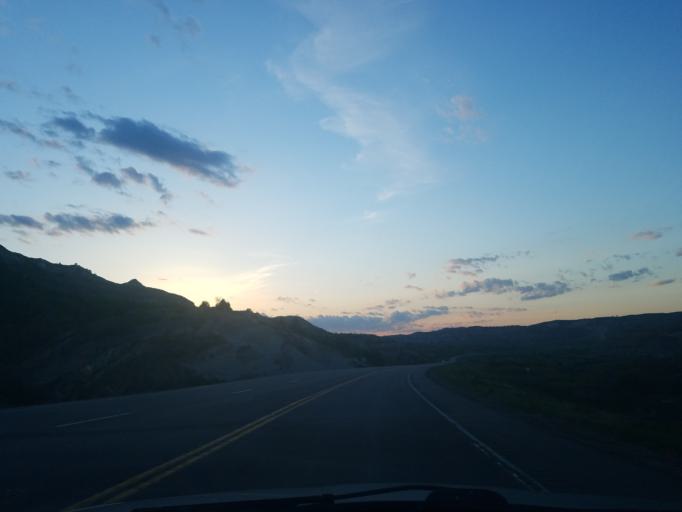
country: US
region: North Dakota
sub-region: McKenzie County
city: Watford City
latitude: 47.5744
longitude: -103.2445
